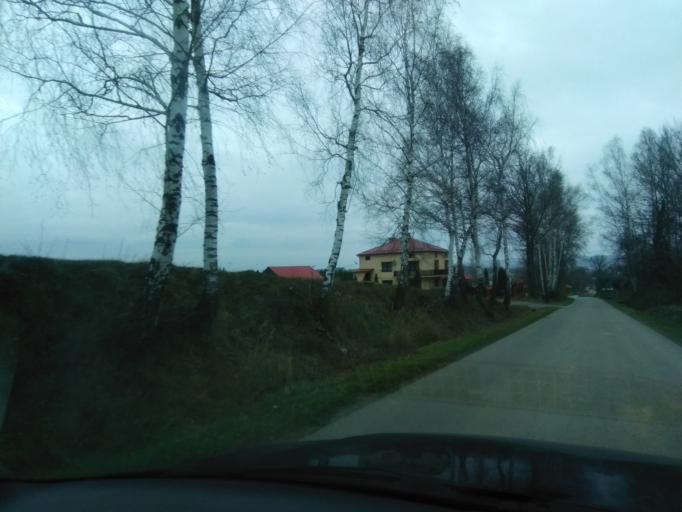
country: PL
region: Subcarpathian Voivodeship
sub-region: Powiat strzyzowski
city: Wysoka Strzyzowska
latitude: 49.8399
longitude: 21.7753
